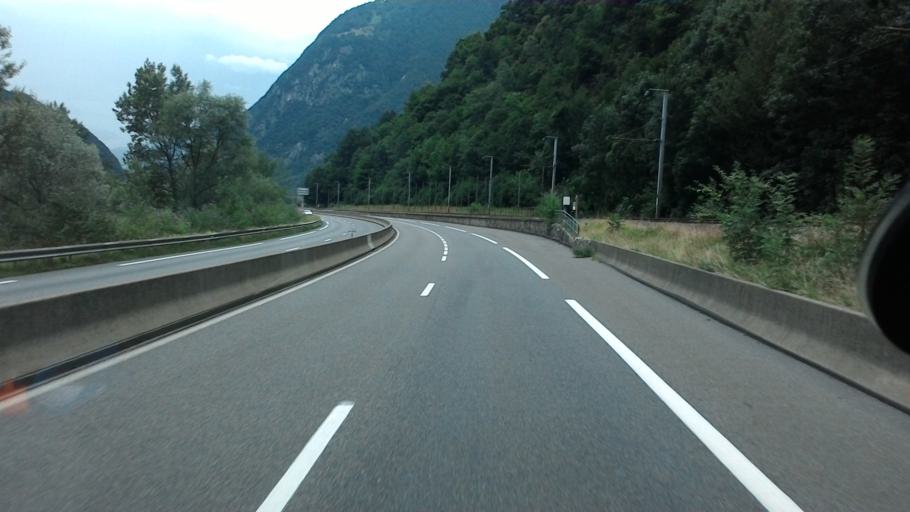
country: FR
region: Rhone-Alpes
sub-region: Departement de la Savoie
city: Aigueblanche
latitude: 45.5507
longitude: 6.4690
